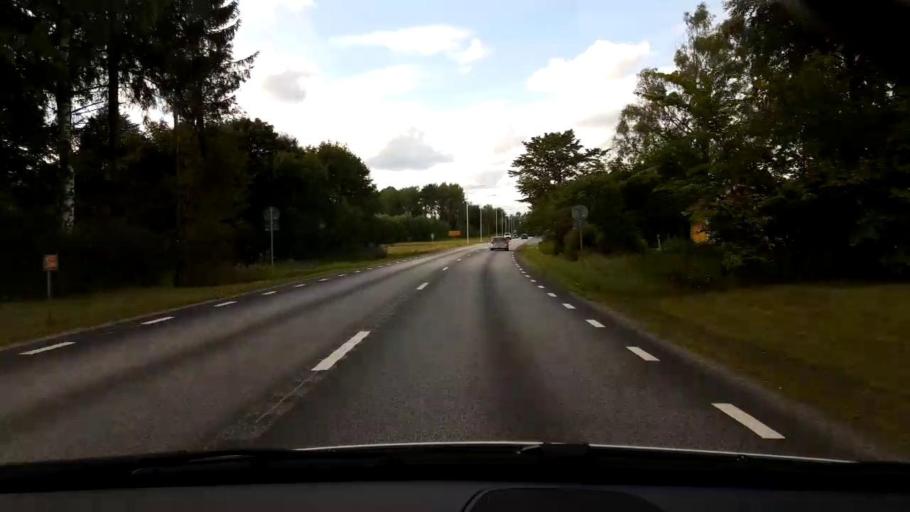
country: SE
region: Joenkoeping
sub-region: Savsjo Kommun
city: Vrigstad
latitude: 57.3601
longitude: 14.4583
